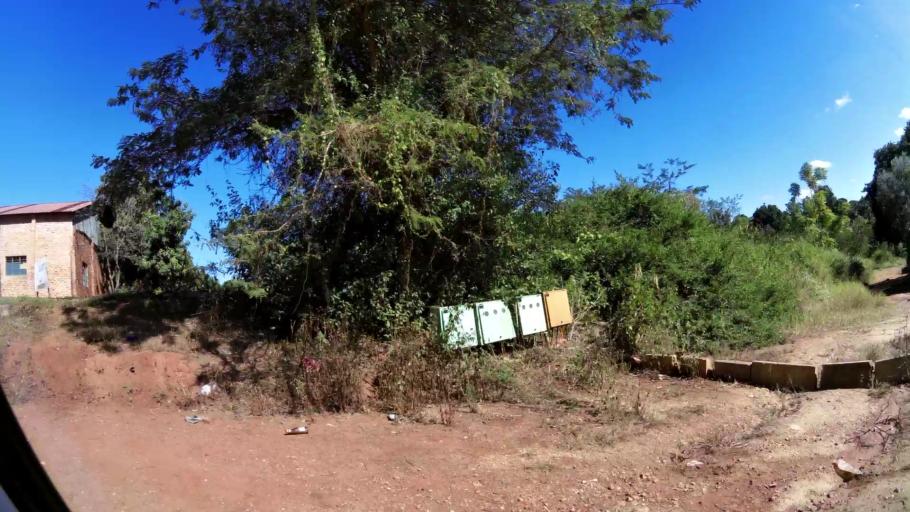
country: ZA
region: Limpopo
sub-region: Mopani District Municipality
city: Tzaneen
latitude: -23.8192
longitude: 30.1553
